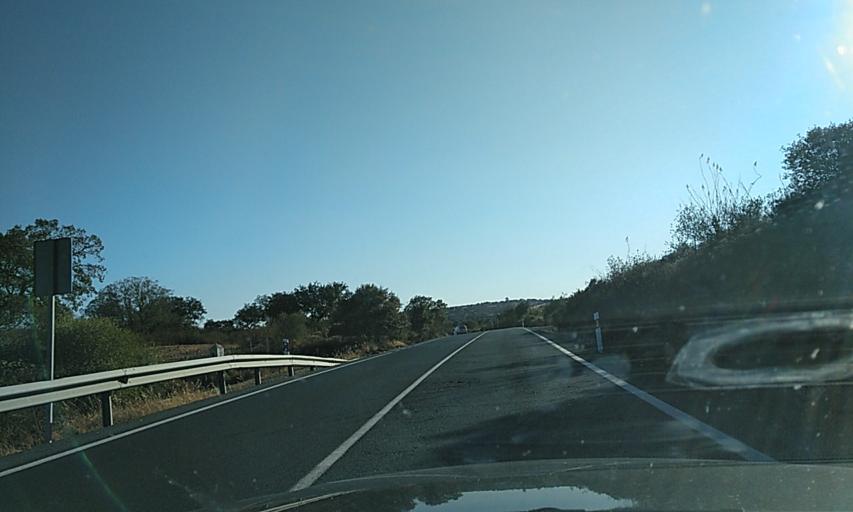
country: ES
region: Andalusia
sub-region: Provincia de Huelva
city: Alosno
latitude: 37.5413
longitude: -7.1290
